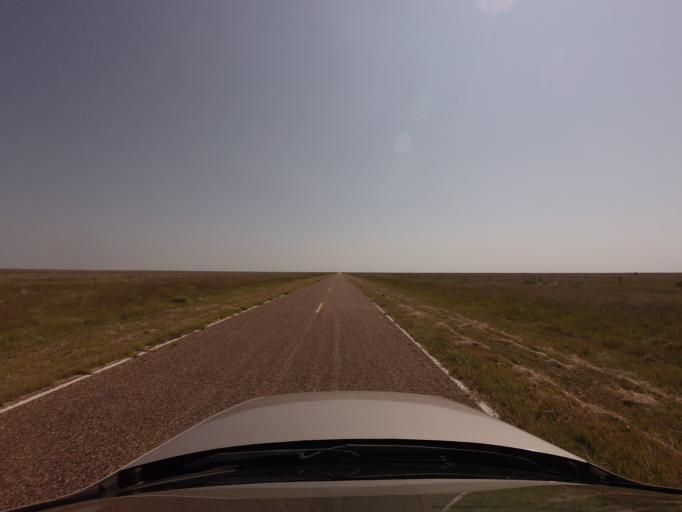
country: US
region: New Mexico
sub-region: Curry County
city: Cannon Air Force Base
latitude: 34.6333
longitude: -103.4579
